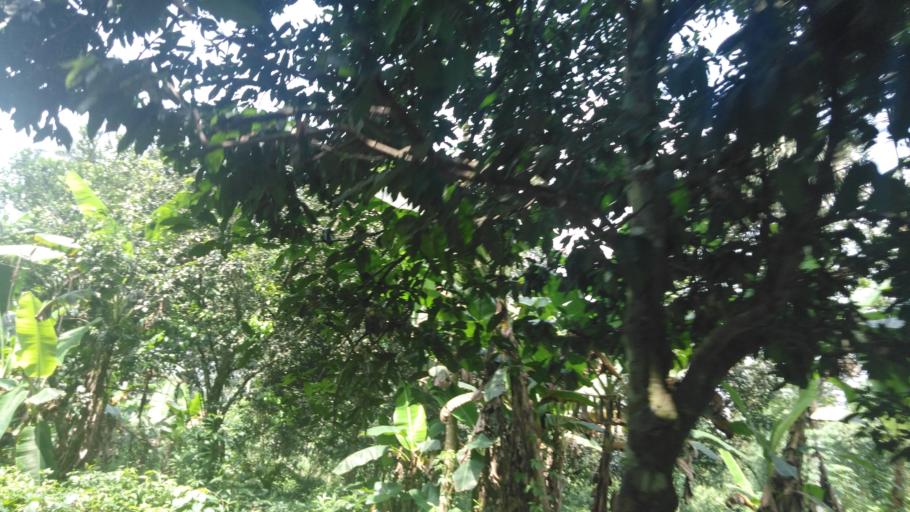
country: NG
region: Abia
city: Aba
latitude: 5.0484
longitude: 7.2400
